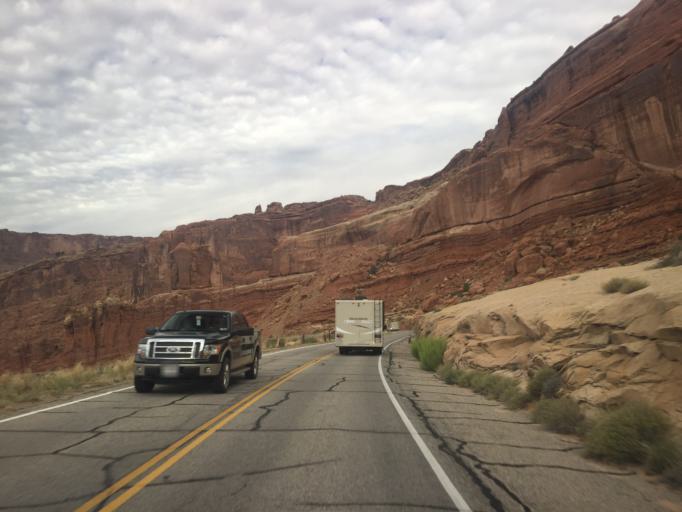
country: US
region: Utah
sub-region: Grand County
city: Moab
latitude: 38.6187
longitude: -109.6125
